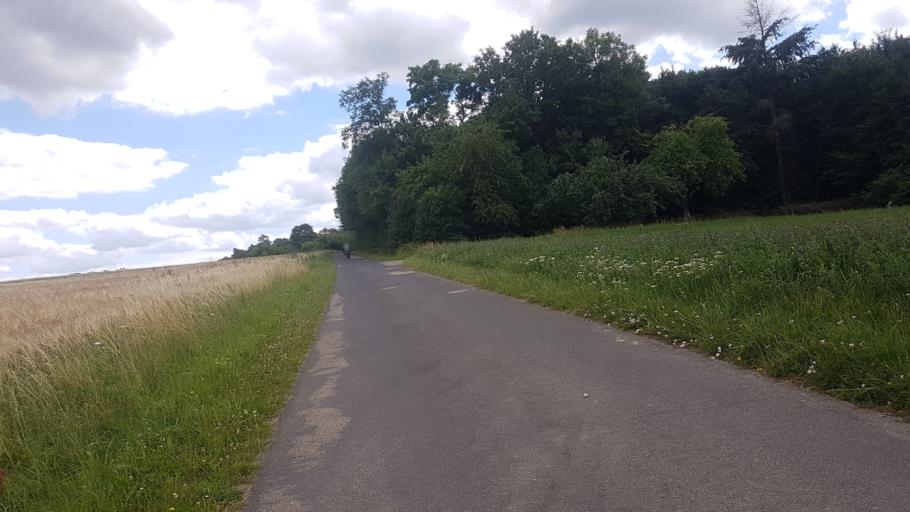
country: DE
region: Baden-Wuerttemberg
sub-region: Regierungsbezirk Stuttgart
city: Assamstadt
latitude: 49.4308
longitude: 9.7453
